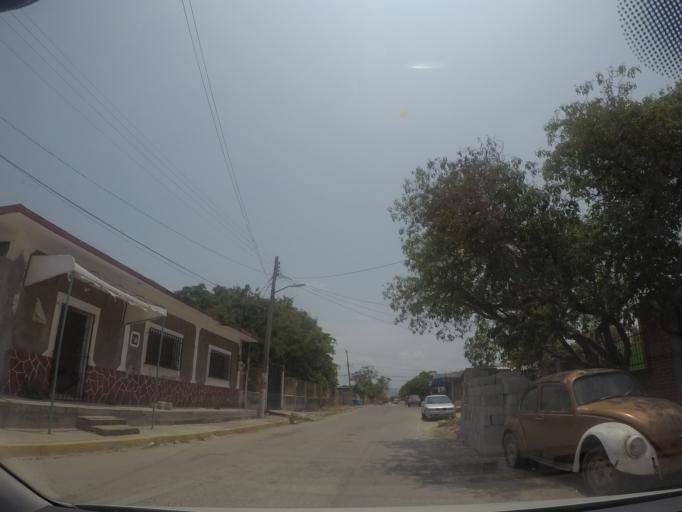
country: MX
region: Oaxaca
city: Asuncion Ixtaltepec
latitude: 16.5059
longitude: -95.0632
